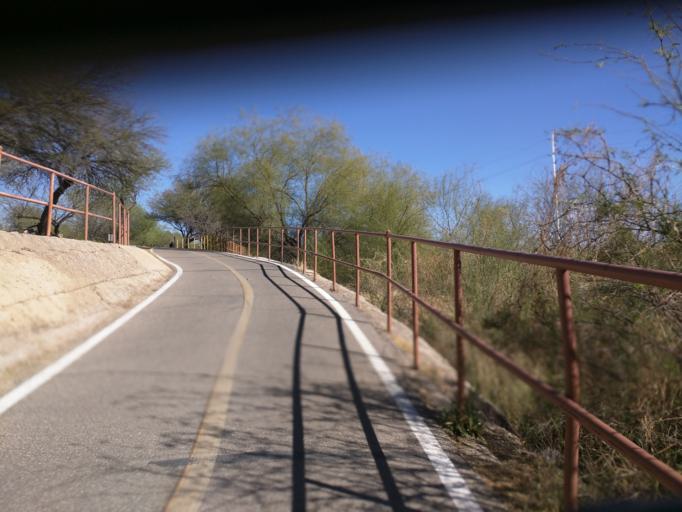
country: US
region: Arizona
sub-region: Pima County
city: Flowing Wells
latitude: 32.2949
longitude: -110.9949
